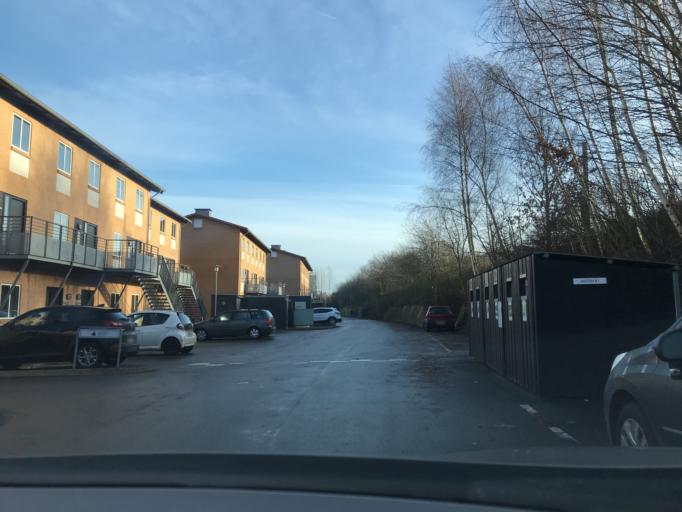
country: DK
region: South Denmark
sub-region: Sonderborg Kommune
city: Dybbol
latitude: 54.9150
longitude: 9.7701
